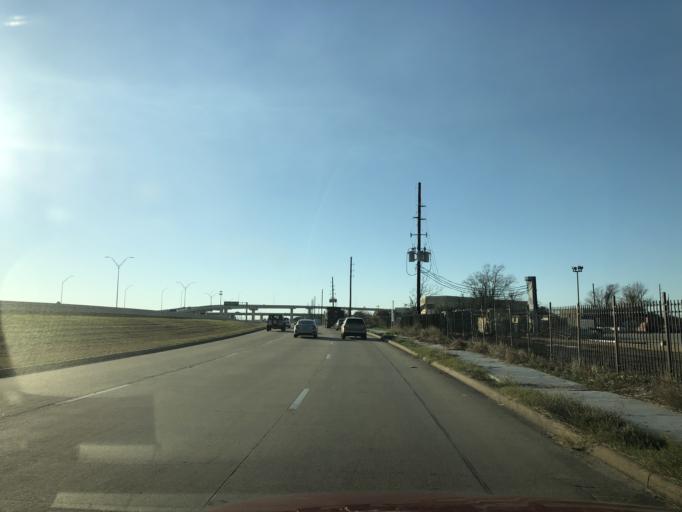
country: US
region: Texas
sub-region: Fort Bend County
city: Cinco Ranch
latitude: 29.7015
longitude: -95.7688
